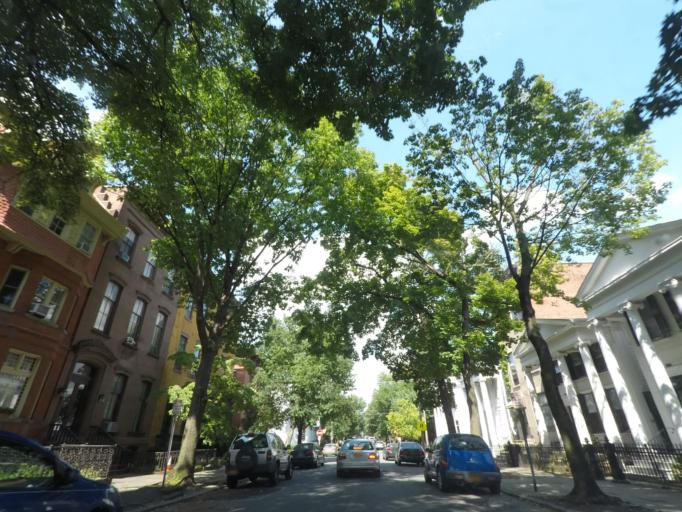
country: US
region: New York
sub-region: Rensselaer County
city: Troy
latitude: 42.7248
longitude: -73.6928
